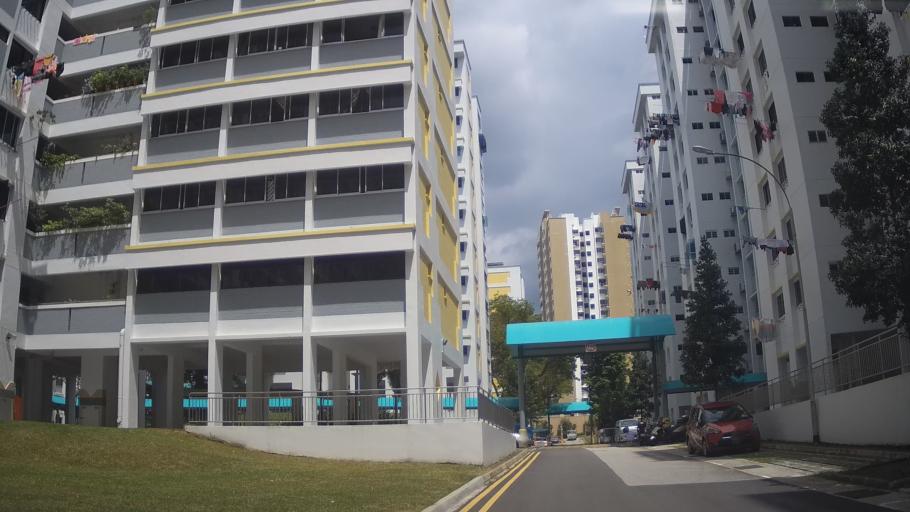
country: MY
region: Johor
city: Johor Bahru
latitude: 1.3816
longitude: 103.7676
